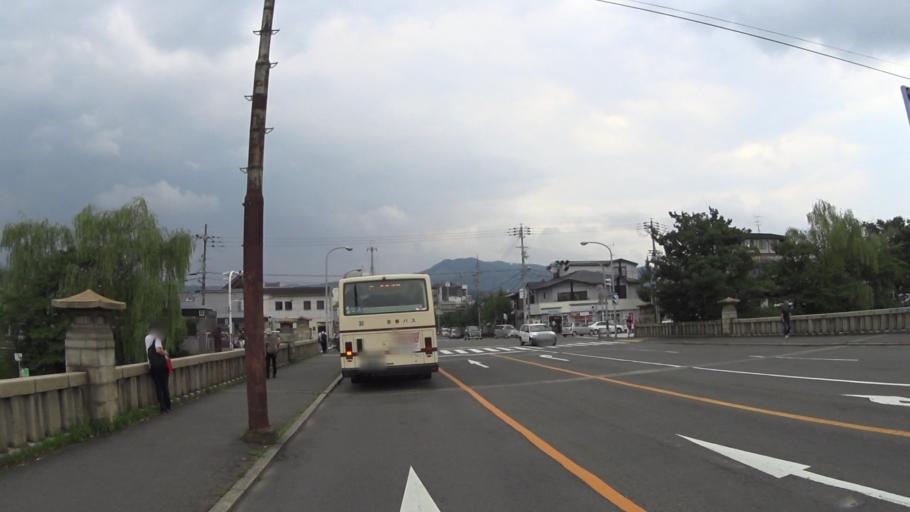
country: JP
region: Kyoto
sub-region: Kyoto-shi
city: Kamigyo-ku
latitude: 35.0291
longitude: 135.7716
